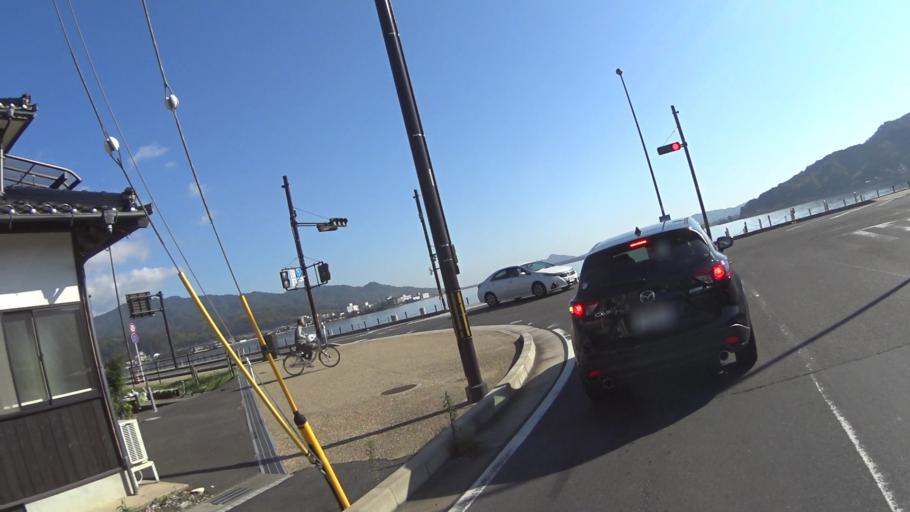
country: JP
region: Kyoto
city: Miyazu
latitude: 35.4390
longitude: 135.1938
